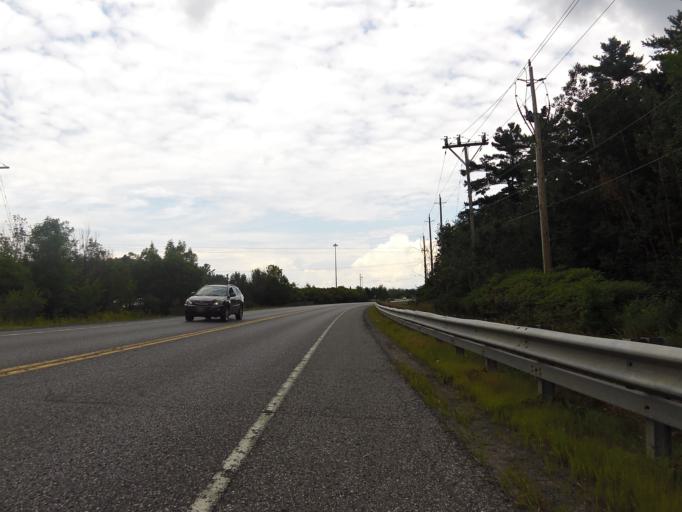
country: CA
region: Ontario
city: Bells Corners
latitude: 45.3208
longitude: -75.8047
